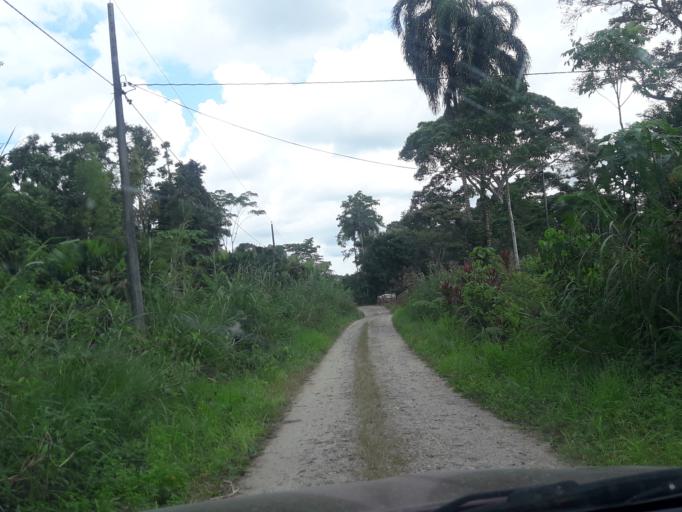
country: EC
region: Napo
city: Tena
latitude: -1.0959
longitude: -77.6757
